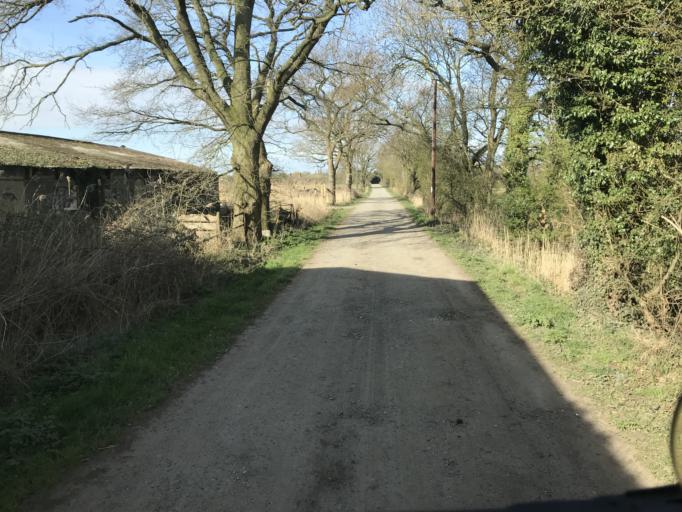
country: GB
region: England
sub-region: Lincolnshire
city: Market Rasen
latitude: 53.3910
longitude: -0.3226
